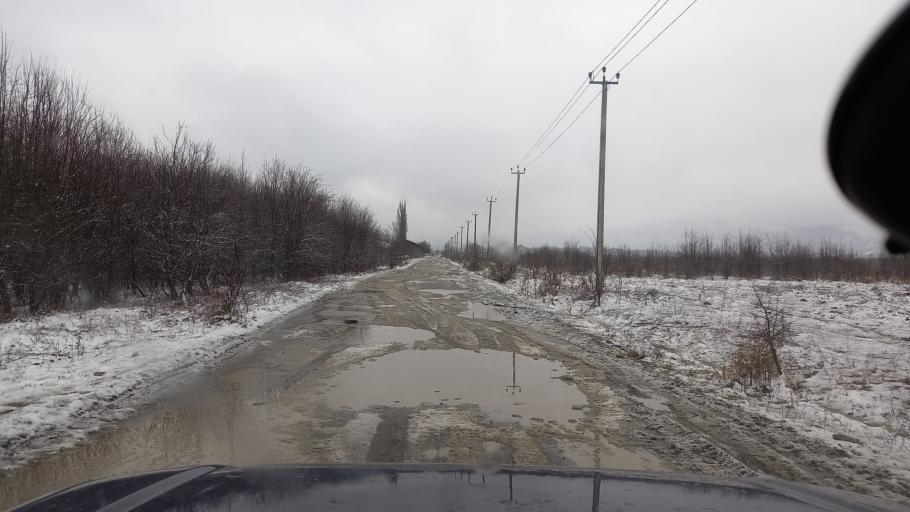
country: RU
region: Adygeya
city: Kamennomostskiy
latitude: 44.2268
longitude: 40.1844
